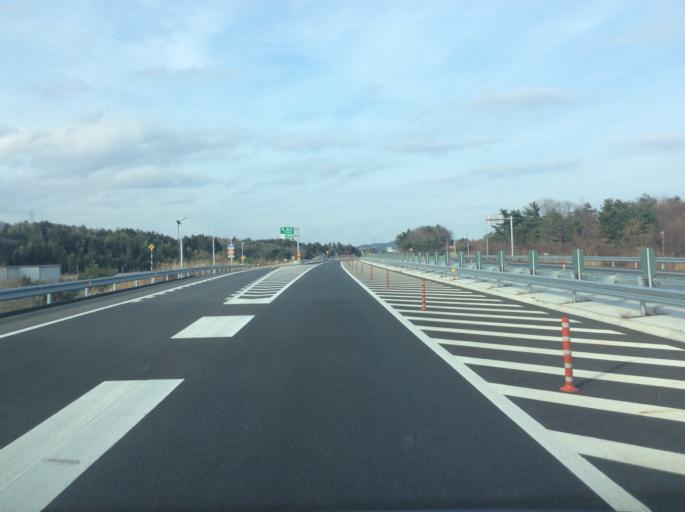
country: JP
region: Fukushima
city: Namie
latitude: 37.3732
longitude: 140.9663
